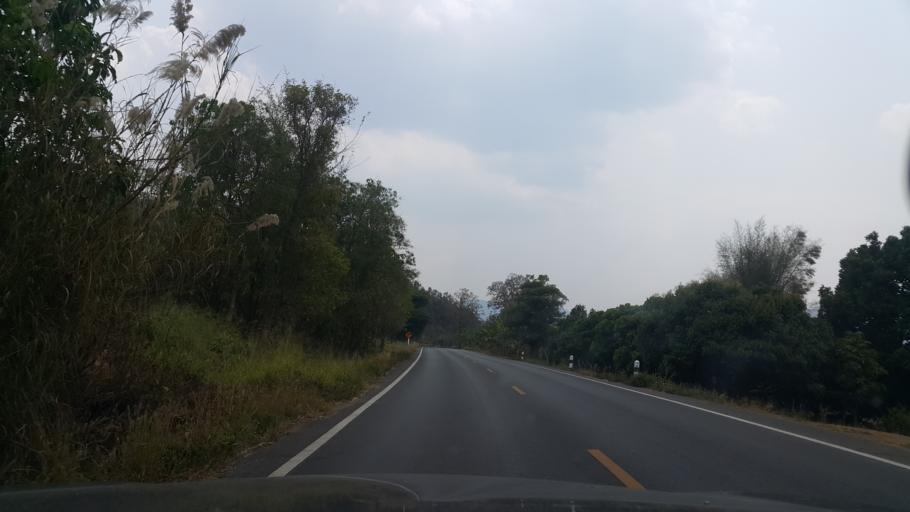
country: TH
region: Lamphun
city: Thung Hua Chang
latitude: 18.1039
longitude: 99.0154
